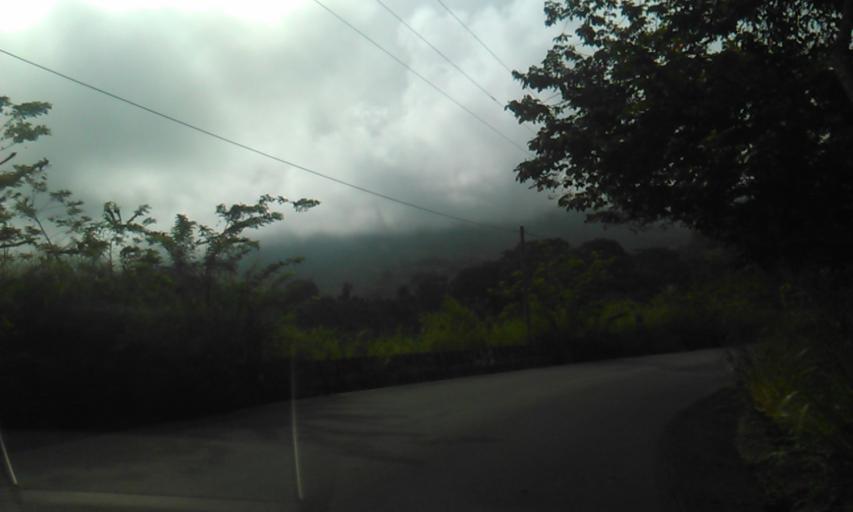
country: CO
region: Quindio
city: Cordoba
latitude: 4.4077
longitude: -75.7263
